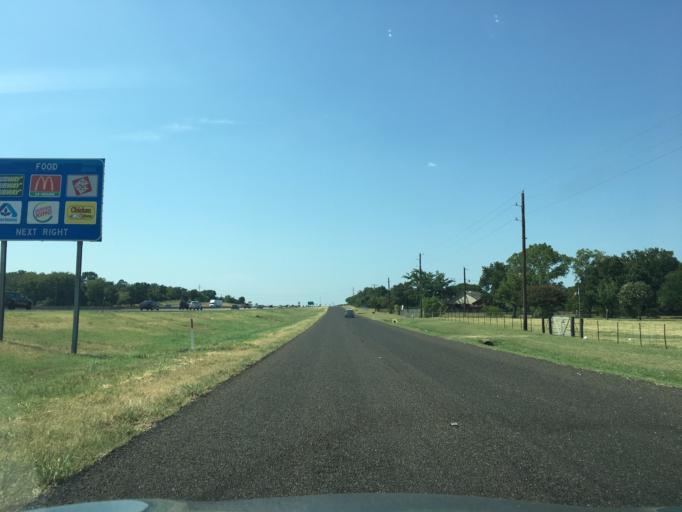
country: US
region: Texas
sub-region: Tarrant County
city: Kennedale
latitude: 32.6384
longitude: -97.1793
